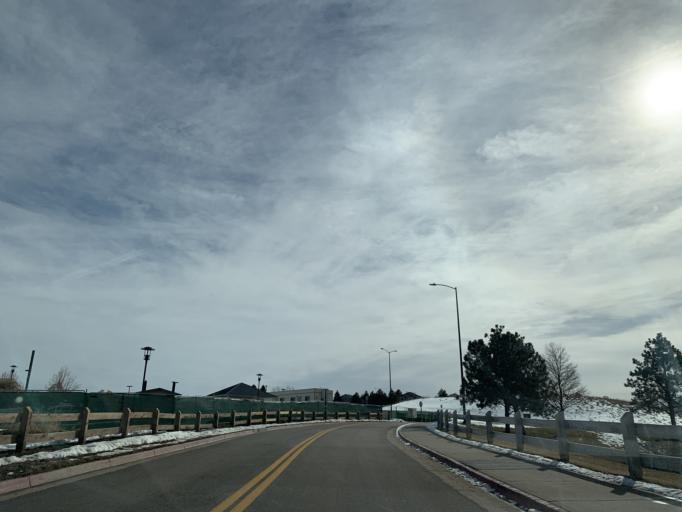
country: US
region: Colorado
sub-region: Douglas County
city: Carriage Club
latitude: 39.5416
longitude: -104.9178
